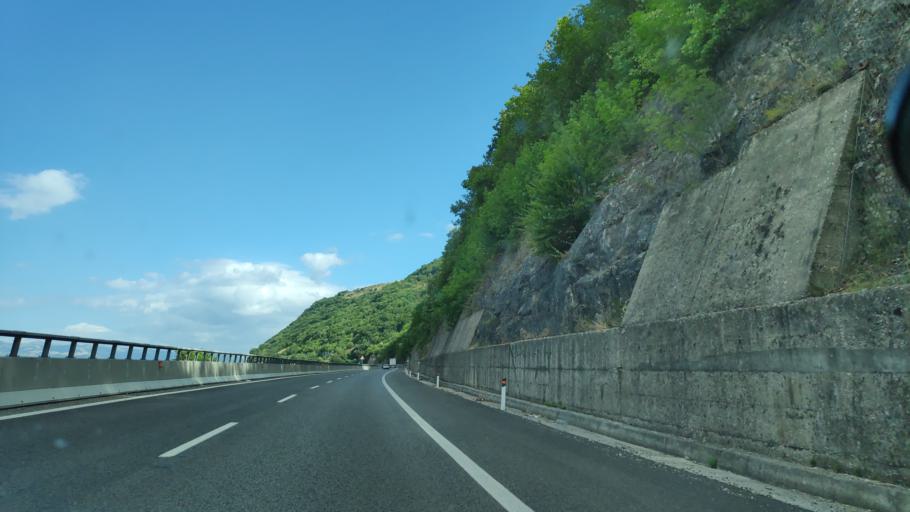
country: IT
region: Campania
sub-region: Provincia di Salerno
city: Sicignano degli Alburni
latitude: 40.5955
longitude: 15.3216
